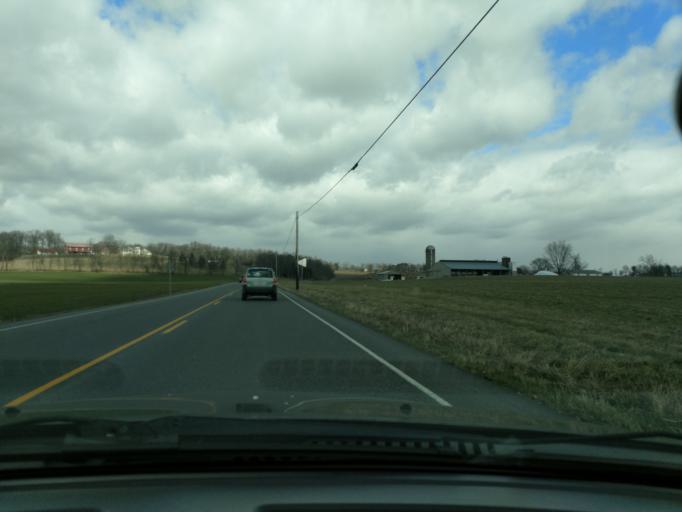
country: US
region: Pennsylvania
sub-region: Lebanon County
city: Myerstown
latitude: 40.3925
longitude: -76.3040
